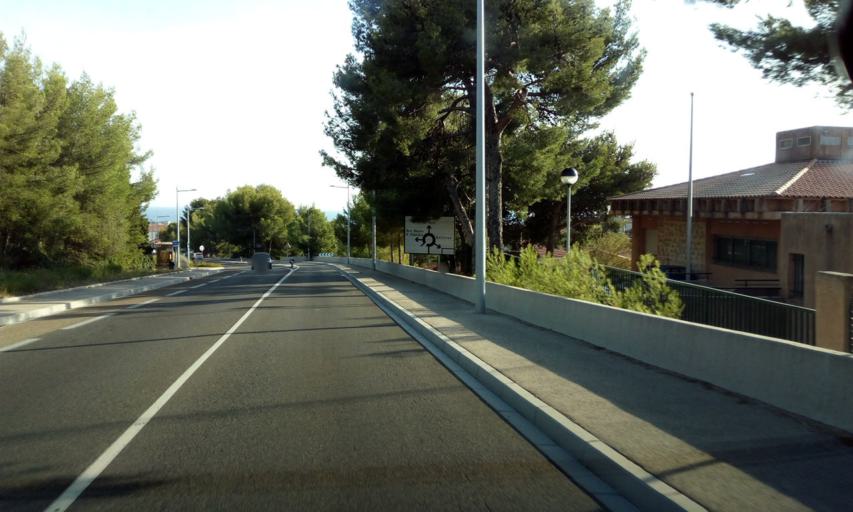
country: FR
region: Provence-Alpes-Cote d'Azur
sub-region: Departement du Var
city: Bandol
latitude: 43.1446
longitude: 5.7477
